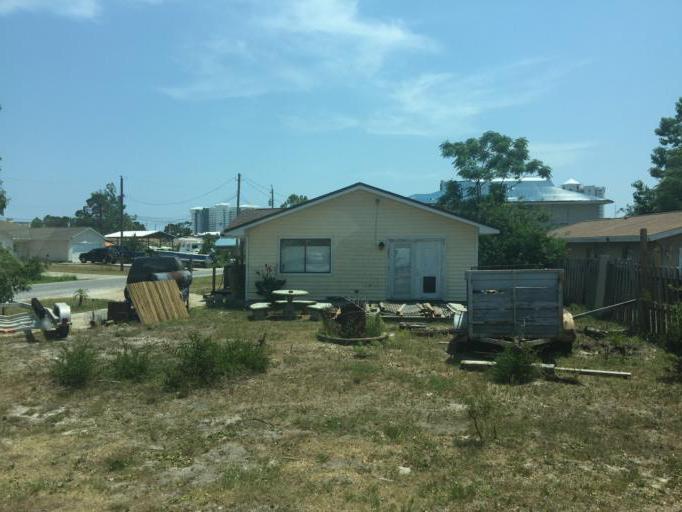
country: US
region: Florida
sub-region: Bay County
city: Lower Grand Lagoon
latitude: 30.1554
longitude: -85.7643
